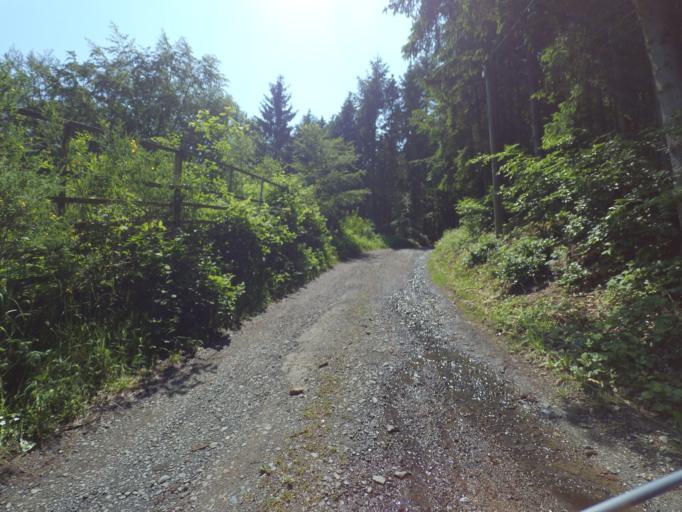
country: DE
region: Rheinland-Pfalz
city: Kalenborn
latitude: 50.2749
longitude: 7.0973
